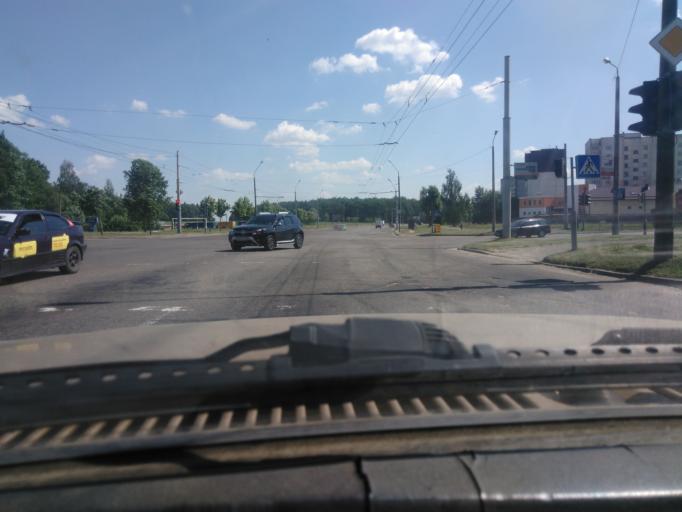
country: BY
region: Mogilev
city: Palykavichy Pyershyya
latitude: 53.9595
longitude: 30.3619
